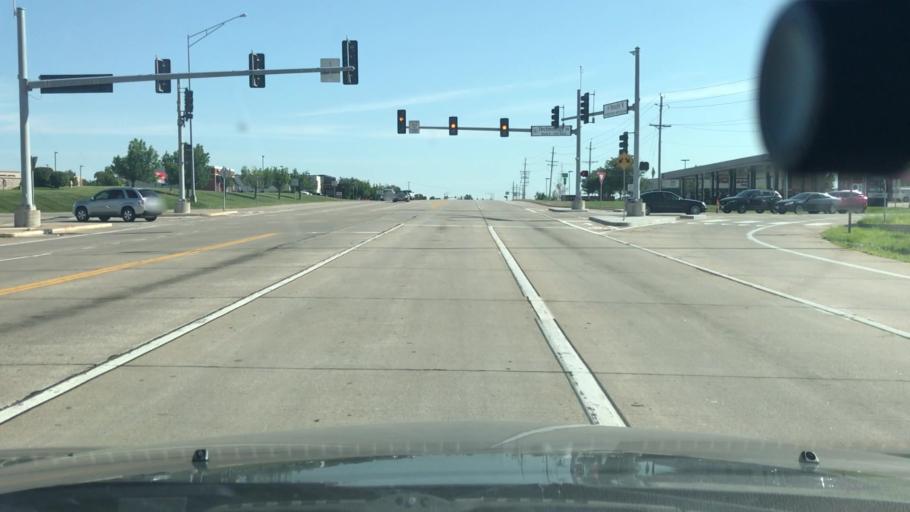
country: US
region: Missouri
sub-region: Saint Charles County
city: Weldon Spring
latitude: 38.7173
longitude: -90.7023
